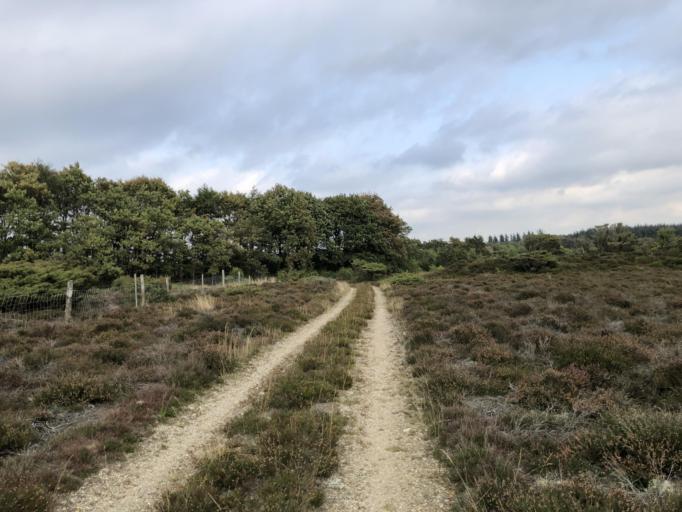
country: DK
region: Central Jutland
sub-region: Holstebro Kommune
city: Ulfborg
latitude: 56.2151
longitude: 8.4283
